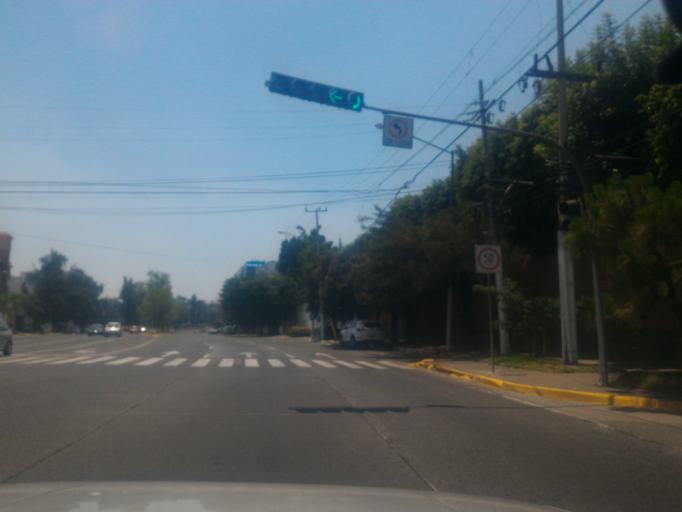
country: MX
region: Jalisco
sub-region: Zapopan
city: Zapopan
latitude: 20.7143
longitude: -103.3852
